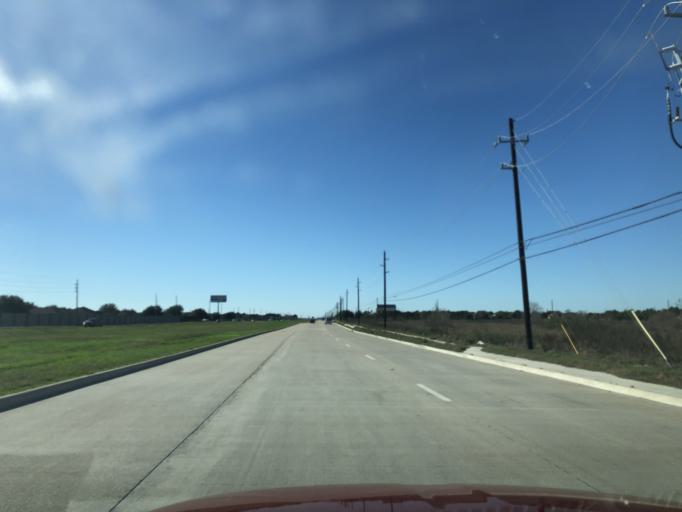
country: US
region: Texas
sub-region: Fort Bend County
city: Cinco Ranch
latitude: 29.6969
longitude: -95.8226
